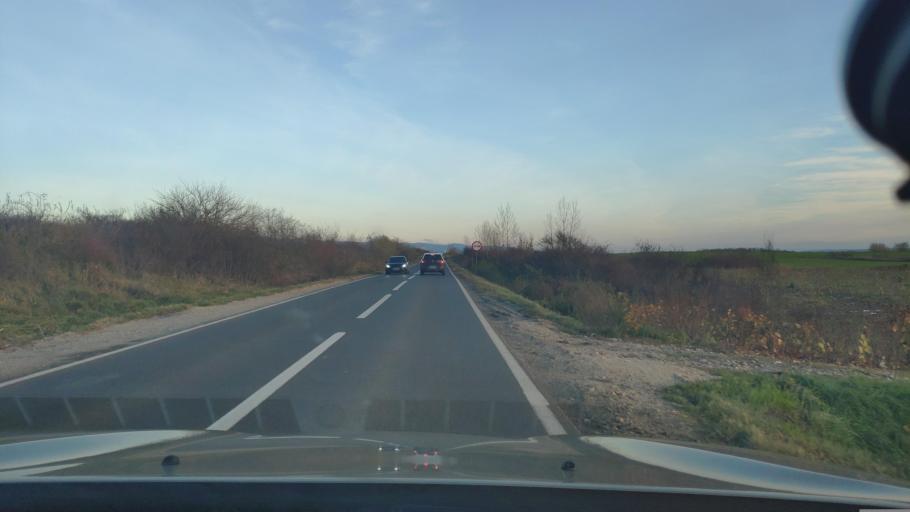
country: RO
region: Satu Mare
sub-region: Comuna Mediesu Aurit
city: Mediesu Aurit
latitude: 47.7699
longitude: 23.1473
